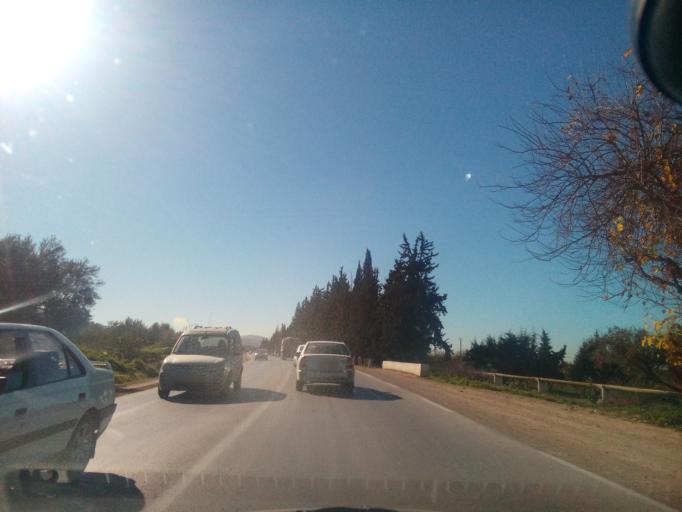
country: DZ
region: Relizane
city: Djidiouia
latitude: 35.9431
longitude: 0.8629
